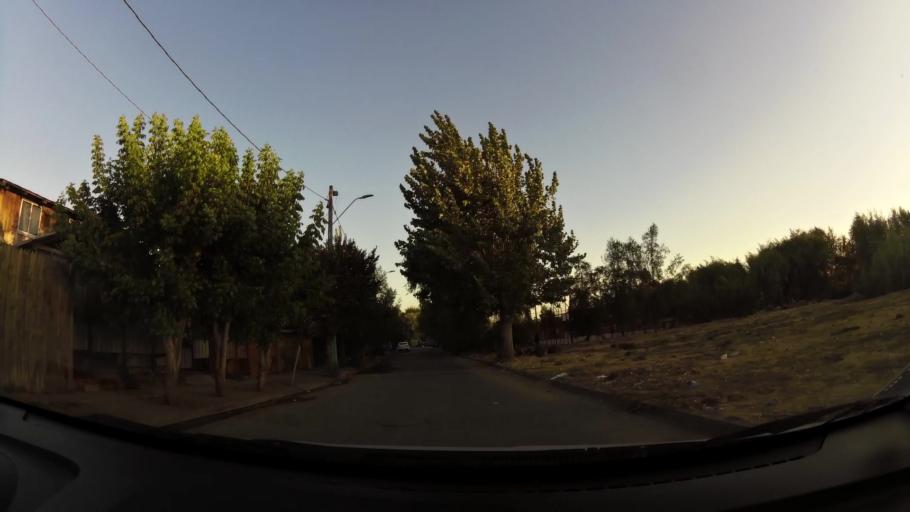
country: CL
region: Maule
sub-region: Provincia de Talca
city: Talca
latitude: -35.4465
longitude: -71.6400
